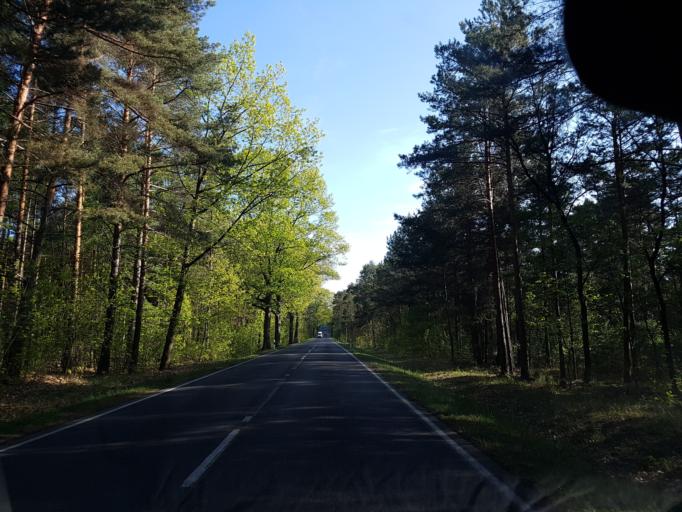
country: DE
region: Brandenburg
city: Altdobern
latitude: 51.6190
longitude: 14.0241
